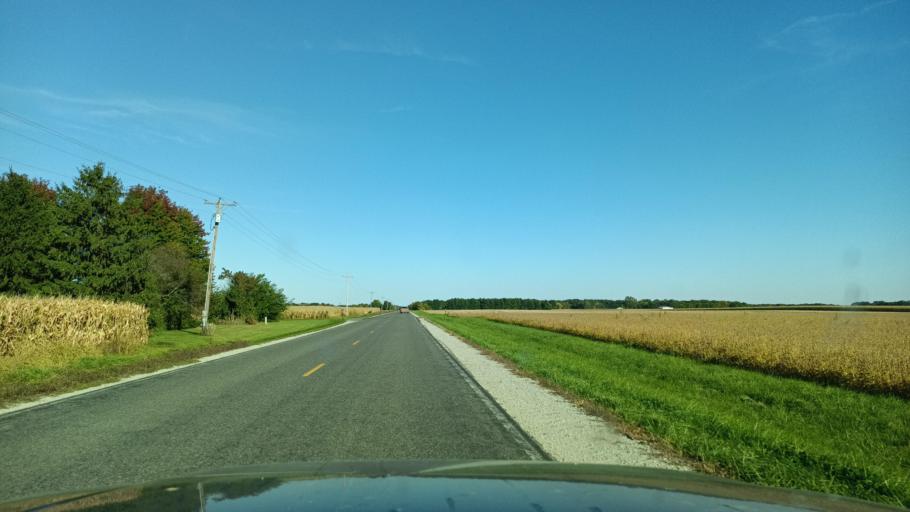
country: US
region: Illinois
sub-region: De Witt County
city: Clinton
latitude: 40.2245
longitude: -88.8470
